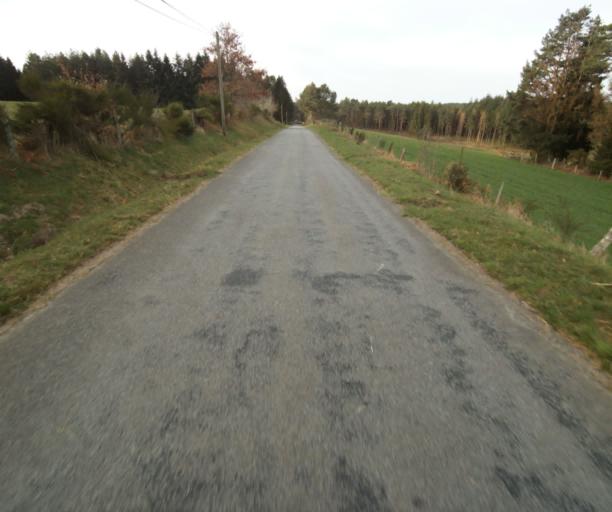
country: FR
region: Limousin
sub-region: Departement de la Correze
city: Treignac
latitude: 45.4643
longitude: 1.8167
